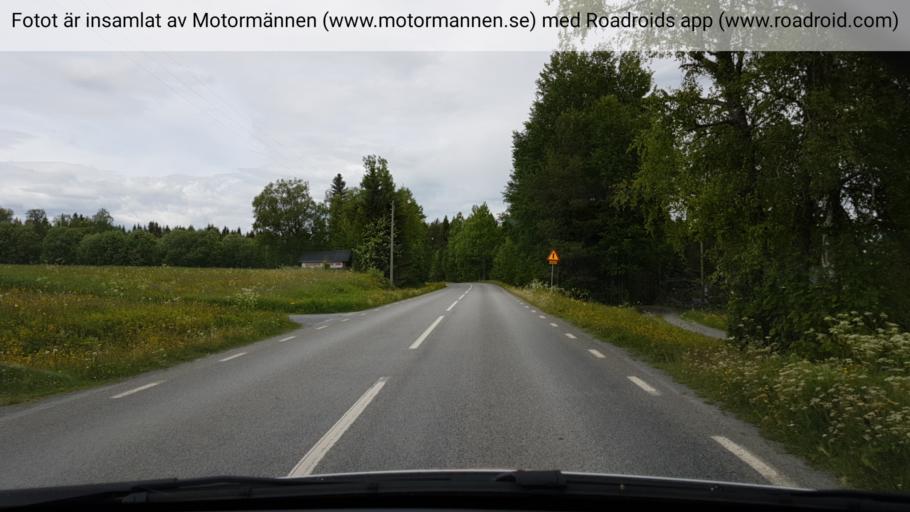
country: SE
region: Jaemtland
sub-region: Krokoms Kommun
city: Krokom
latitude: 63.1494
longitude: 14.1654
